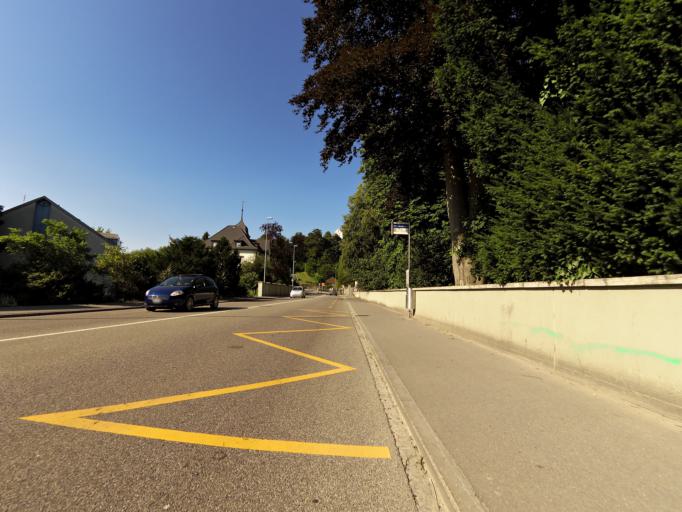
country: CH
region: Aargau
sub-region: Bezirk Lenzburg
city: Niederlenz
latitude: 47.4164
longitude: 8.1672
